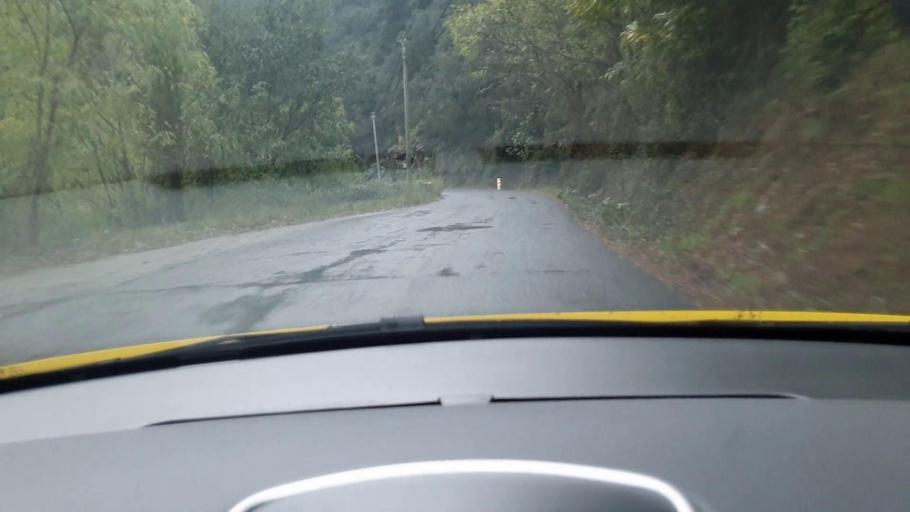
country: FR
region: Languedoc-Roussillon
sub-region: Departement du Gard
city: Sumene
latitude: 44.0037
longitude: 3.7110
